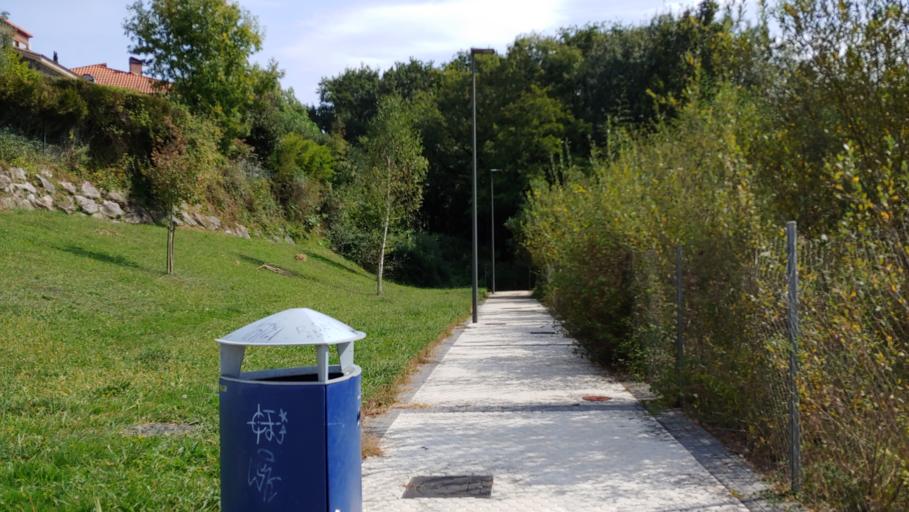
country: ES
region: Basque Country
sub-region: Provincia de Guipuzcoa
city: Lasarte
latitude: 43.3024
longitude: -2.0159
